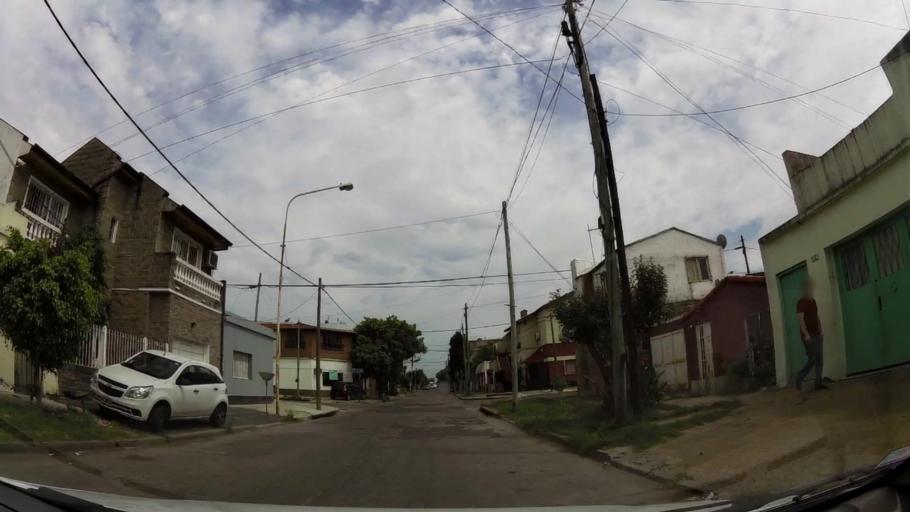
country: AR
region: Buenos Aires F.D.
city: Villa Lugano
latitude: -34.6862
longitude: -58.5001
